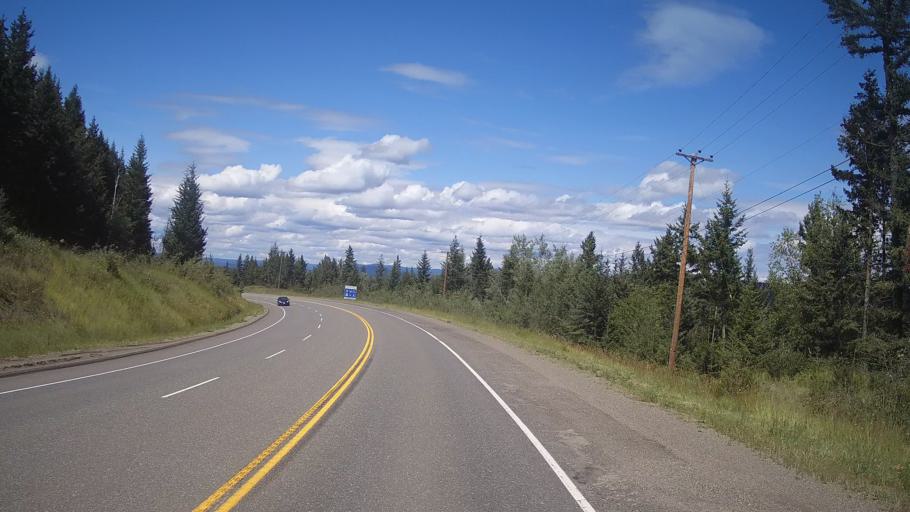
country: CA
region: British Columbia
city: Cache Creek
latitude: 51.6123
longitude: -121.2866
